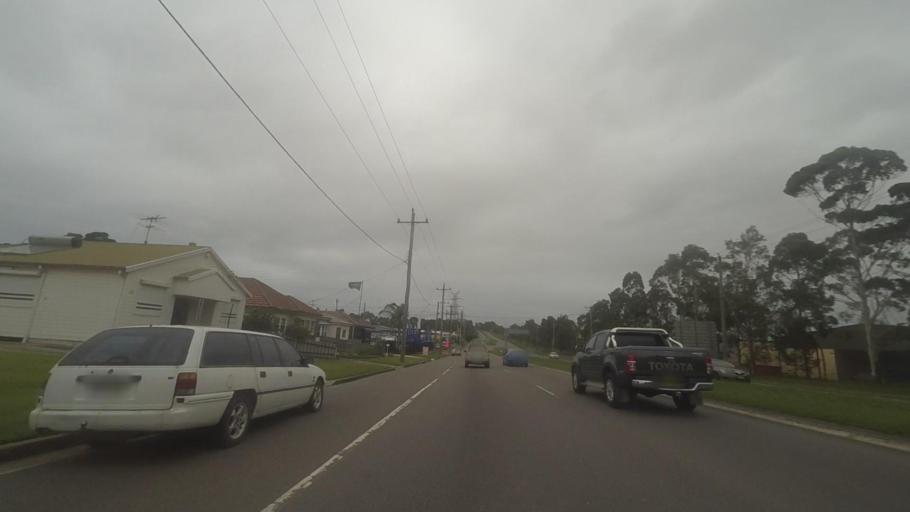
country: AU
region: New South Wales
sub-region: Newcastle
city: Mayfield West
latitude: -32.8722
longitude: 151.7110
